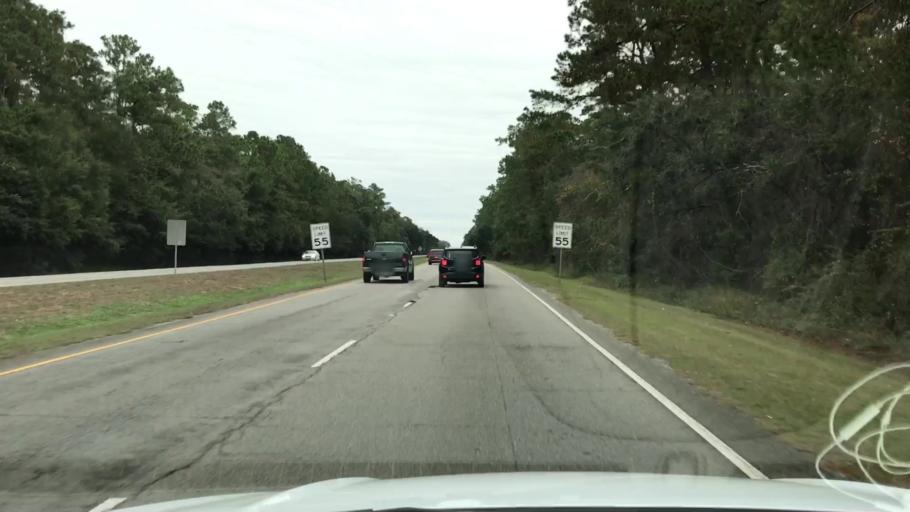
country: US
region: South Carolina
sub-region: Georgetown County
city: Murrells Inlet
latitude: 33.4990
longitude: -79.0839
